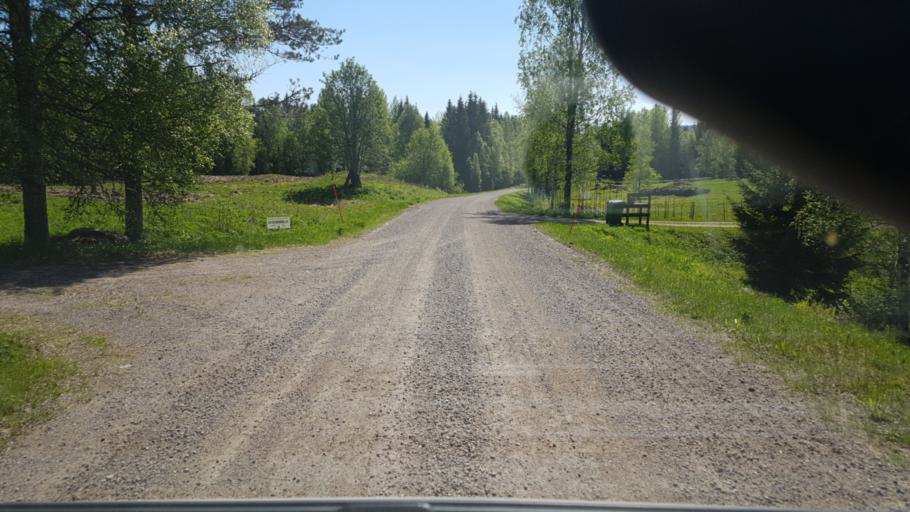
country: SE
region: Vaermland
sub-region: Eda Kommun
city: Charlottenberg
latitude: 59.9959
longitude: 12.5082
